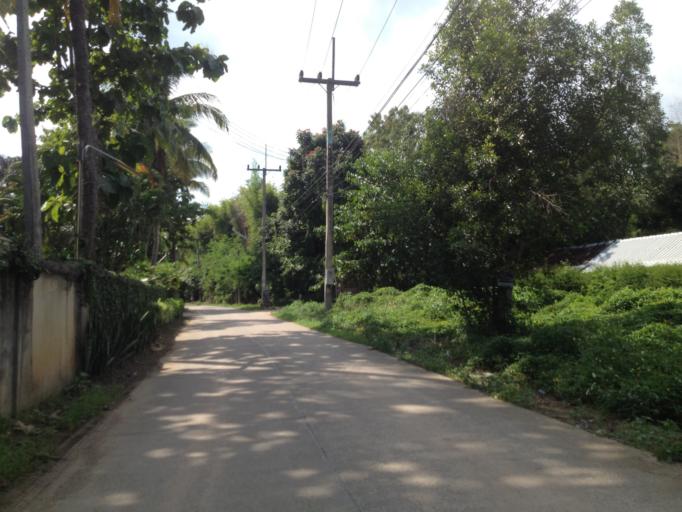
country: TH
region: Chiang Mai
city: Hang Dong
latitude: 18.7392
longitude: 98.9274
